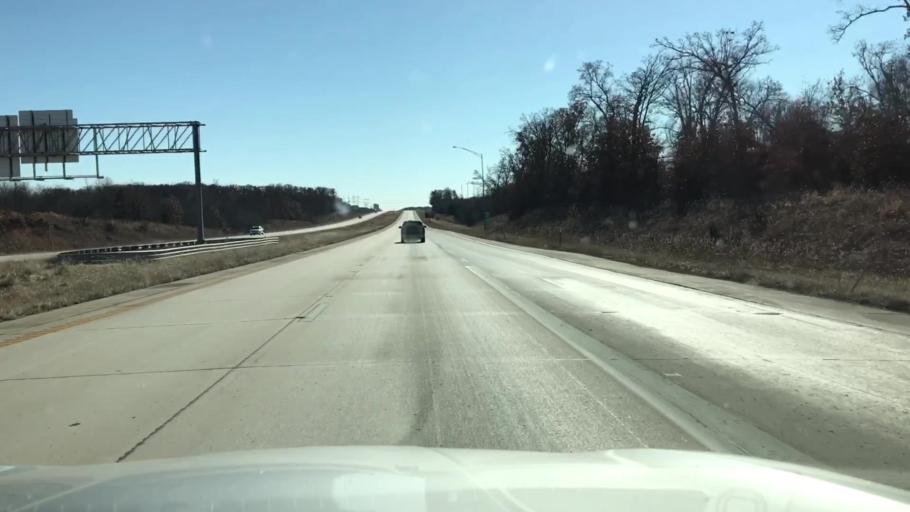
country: US
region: Missouri
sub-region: Jasper County
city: Duenweg
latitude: 37.0502
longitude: -94.4272
